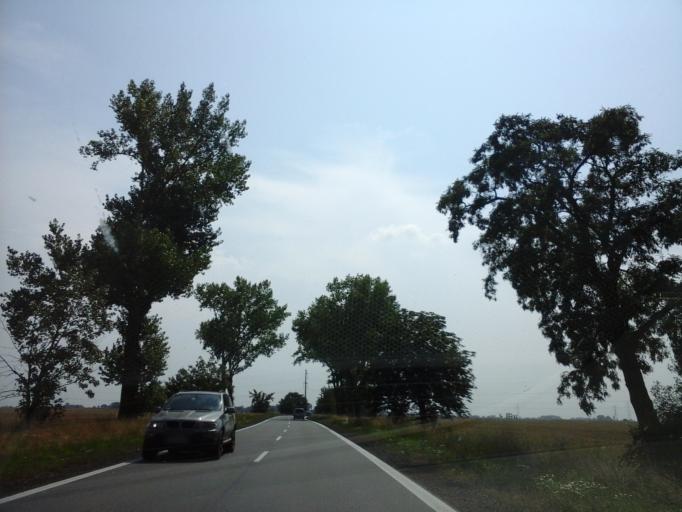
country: PL
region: Lower Silesian Voivodeship
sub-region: Powiat wroclawski
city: Zerniki Wroclawskie
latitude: 51.0131
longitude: 17.0644
